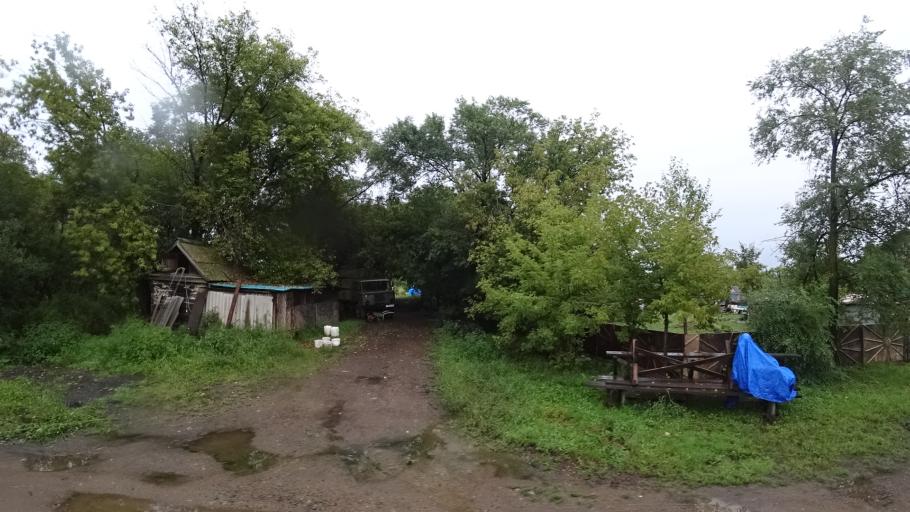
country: RU
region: Primorskiy
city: Monastyrishche
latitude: 44.2575
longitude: 132.4278
